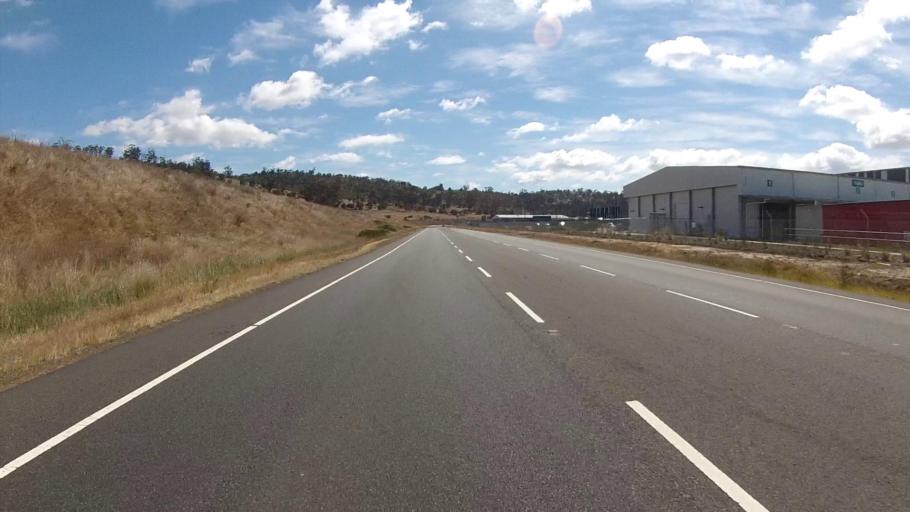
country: AU
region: Tasmania
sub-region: Brighton
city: Bridgewater
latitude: -42.7170
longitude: 147.2258
